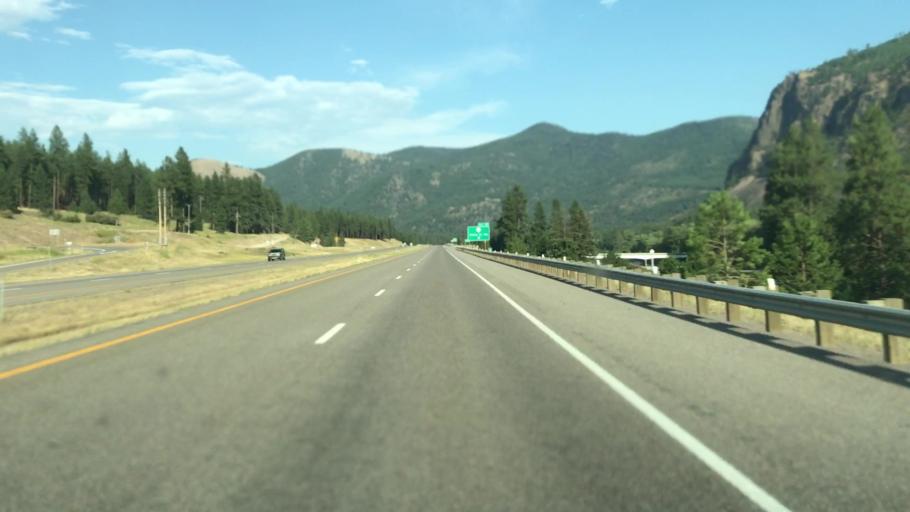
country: US
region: Montana
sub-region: Missoula County
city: Frenchtown
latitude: 46.9952
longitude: -114.4545
